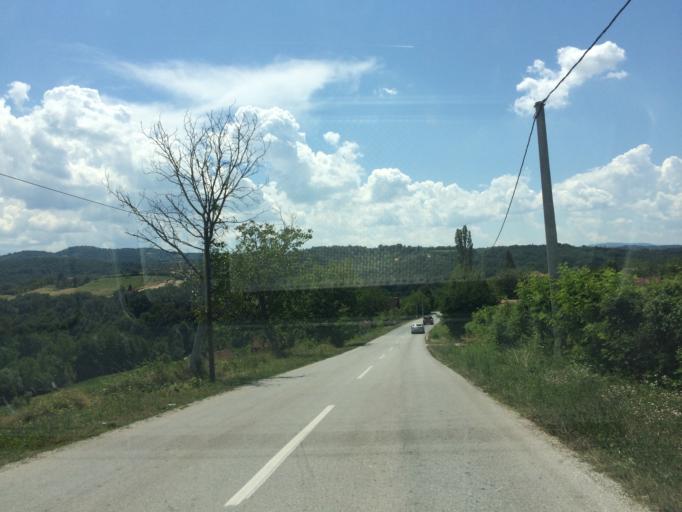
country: RS
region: Central Serbia
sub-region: Kolubarski Okrug
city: Ljig
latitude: 44.2228
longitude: 20.1781
